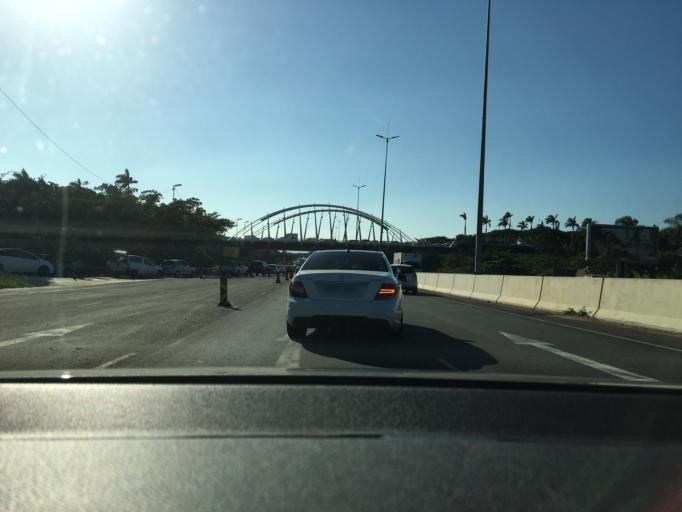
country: ZA
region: KwaZulu-Natal
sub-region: eThekwini Metropolitan Municipality
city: Durban
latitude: -29.7288
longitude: 31.0640
